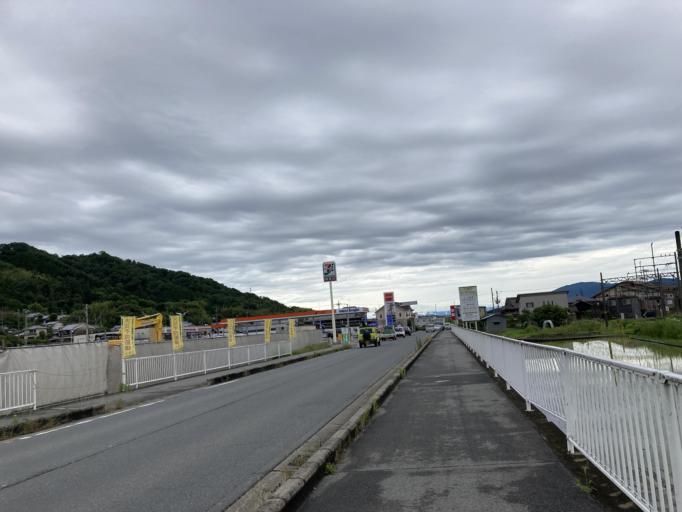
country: JP
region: Nara
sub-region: Ikoma-shi
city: Ikoma
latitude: 34.6256
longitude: 135.7068
